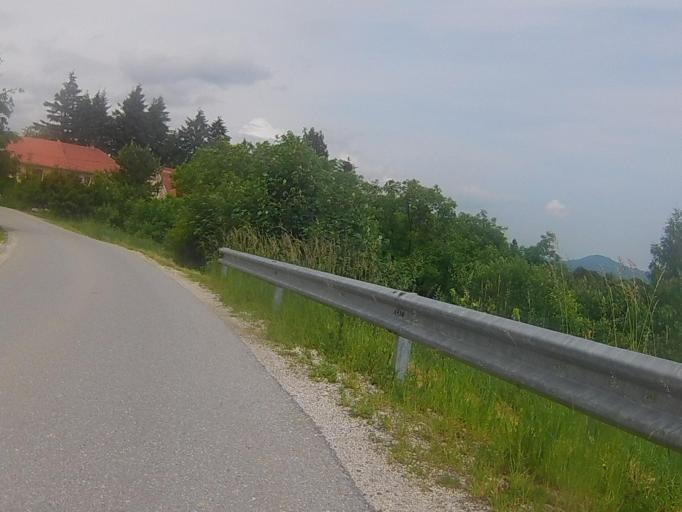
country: SI
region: Maribor
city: Limbus
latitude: 46.5315
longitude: 15.5791
